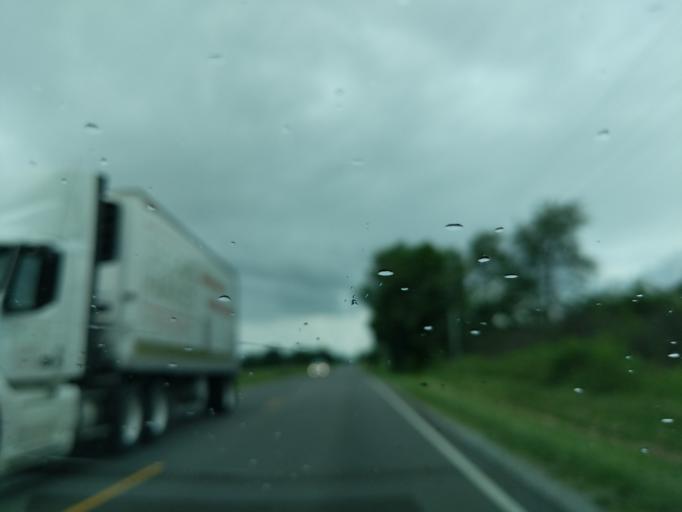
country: US
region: Indiana
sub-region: Madison County
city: Chesterfield
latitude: 40.1049
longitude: -85.6001
